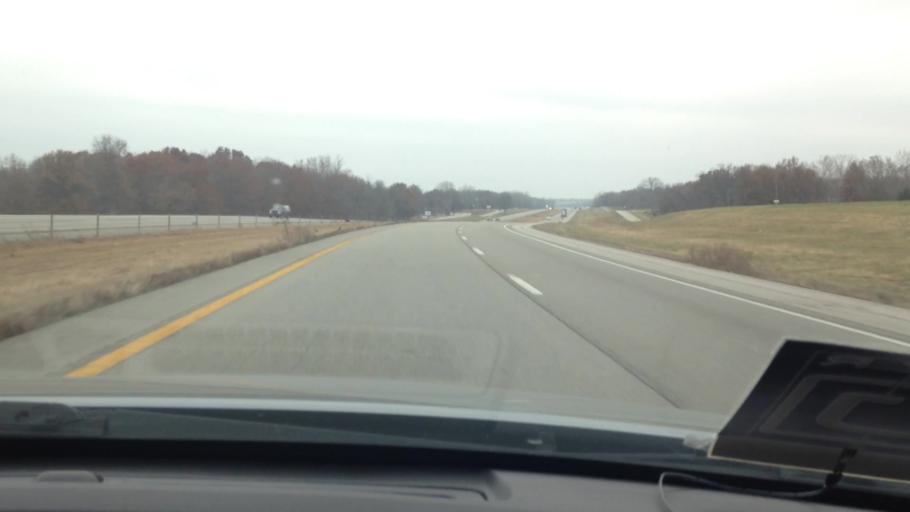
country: US
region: Missouri
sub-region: Cass County
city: Peculiar
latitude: 38.6784
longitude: -94.4195
